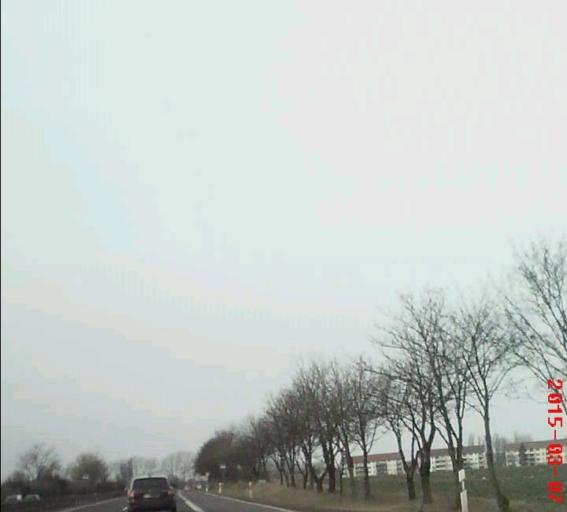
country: DE
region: Thuringia
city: Elxleben
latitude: 51.0351
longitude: 10.9568
